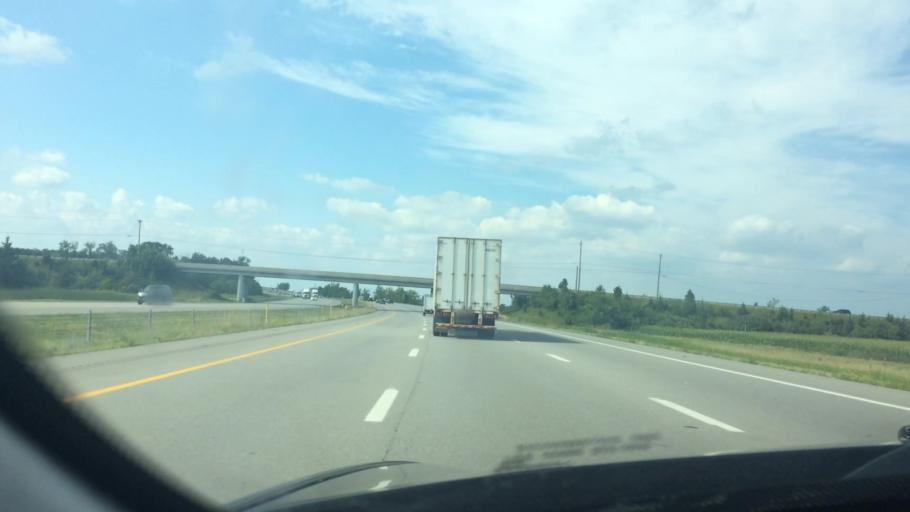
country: US
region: Ohio
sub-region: Wood County
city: Bowling Green
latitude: 41.4270
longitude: -83.6154
